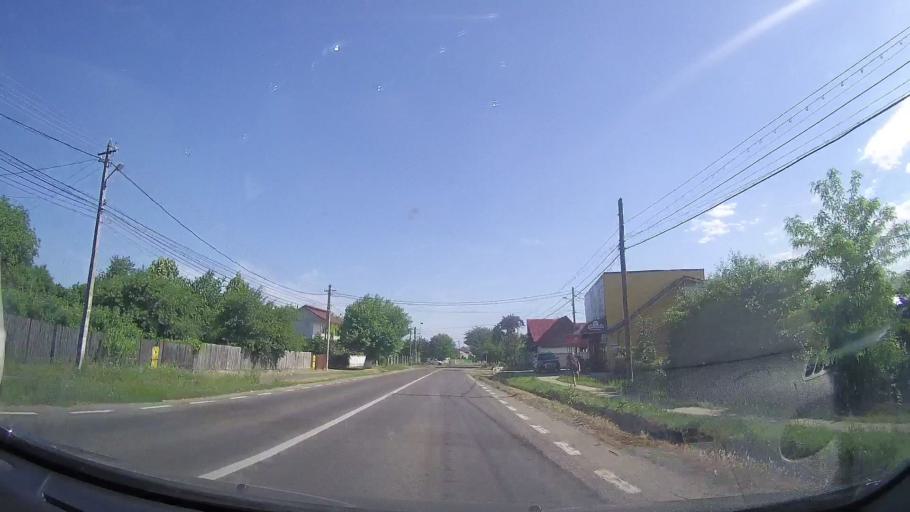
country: RO
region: Prahova
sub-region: Comuna Magurele
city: Magurele
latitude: 45.0983
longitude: 26.0366
